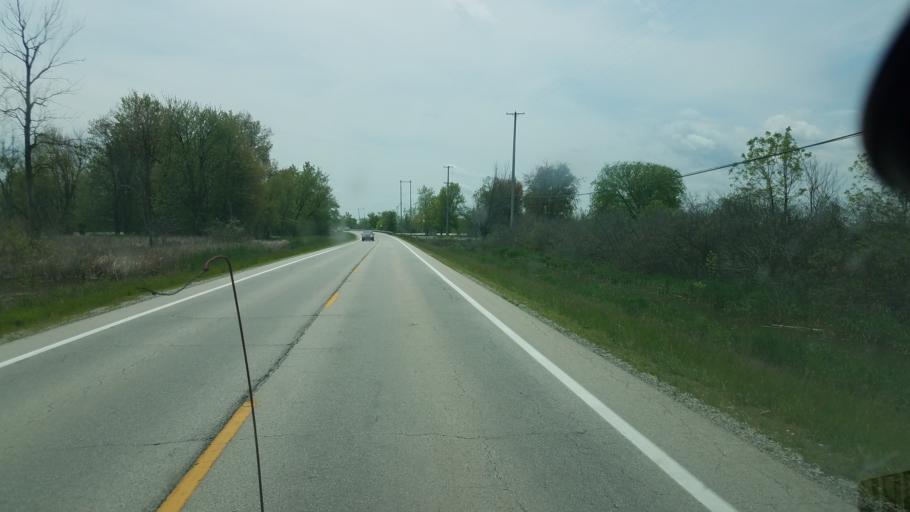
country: US
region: Ohio
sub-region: Ottawa County
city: Oak Harbor
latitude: 41.4549
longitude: -83.0533
